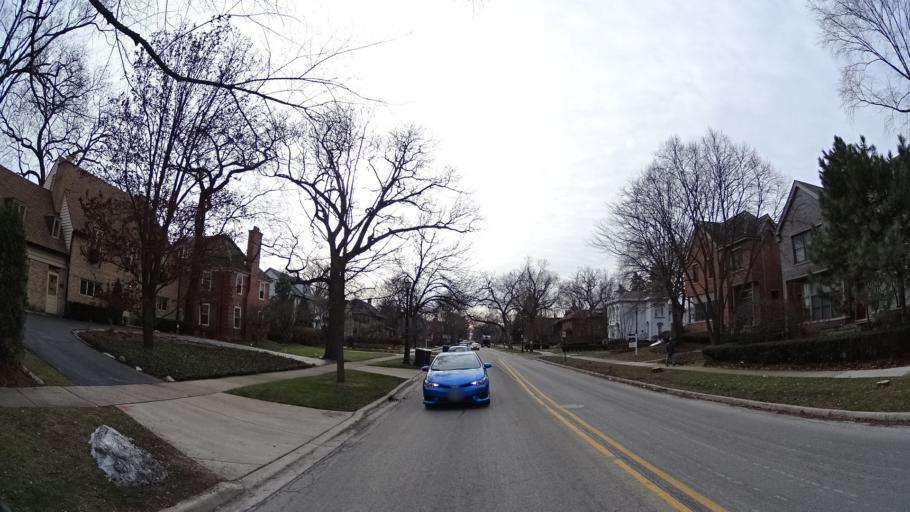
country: US
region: Illinois
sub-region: Cook County
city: Evanston
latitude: 42.0392
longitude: -87.6898
